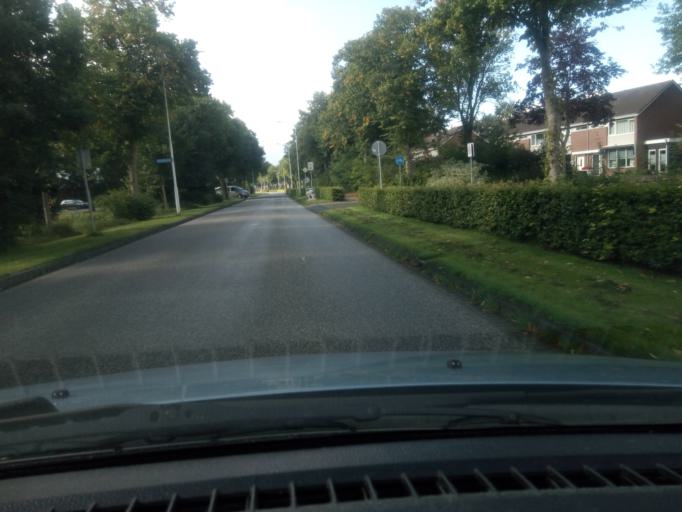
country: NL
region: Friesland
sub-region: Gemeente Achtkarspelen
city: Surhuisterveen
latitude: 53.1836
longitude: 6.1812
